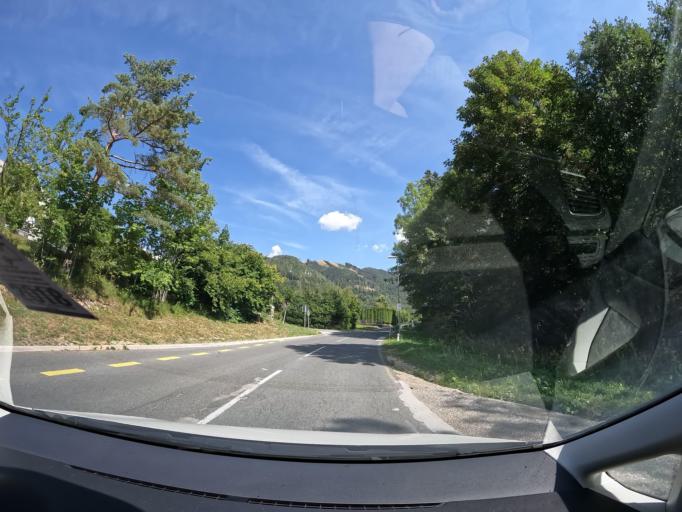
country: AT
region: Carinthia
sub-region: Politischer Bezirk Klagenfurt Land
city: Moosburg
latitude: 46.6624
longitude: 14.1299
